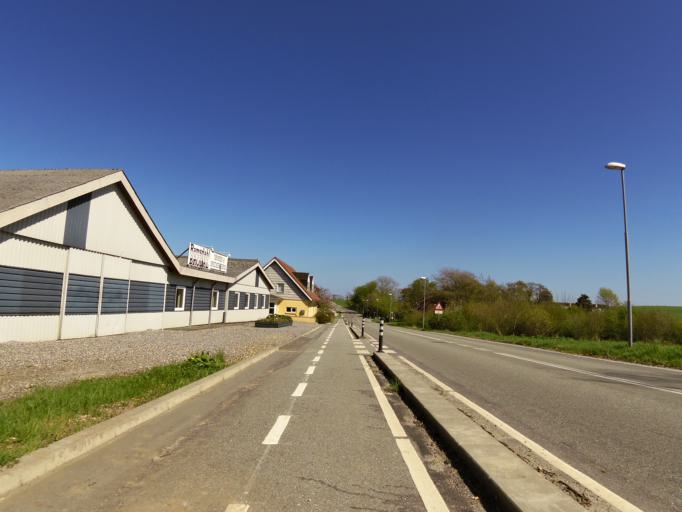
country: DK
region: Central Jutland
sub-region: Holstebro Kommune
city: Vinderup
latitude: 56.6001
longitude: 8.7571
